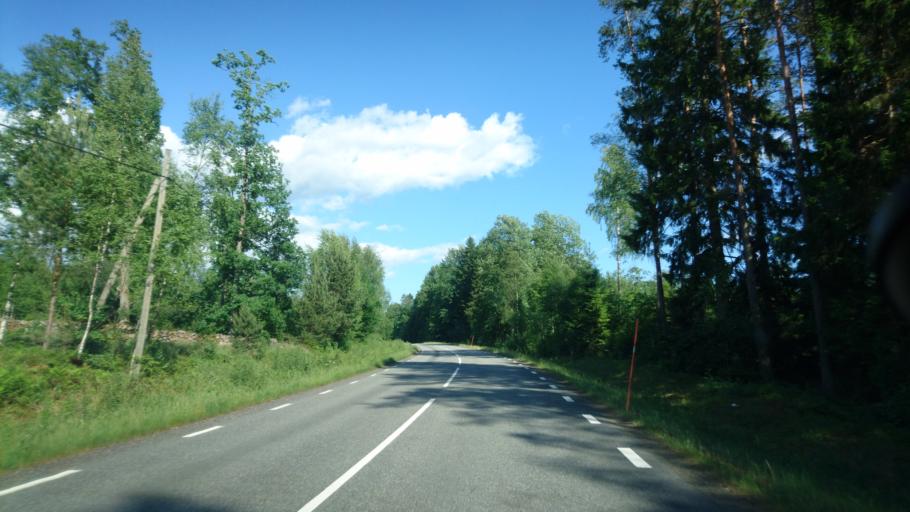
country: SE
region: Kronoberg
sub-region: Almhults Kommun
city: AElmhult
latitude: 56.4811
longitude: 14.1904
